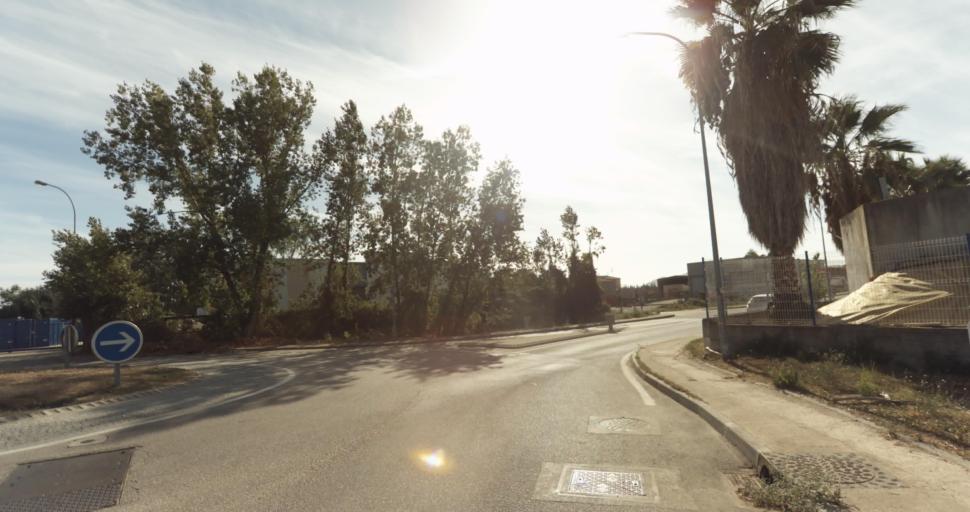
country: FR
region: Corsica
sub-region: Departement de la Corse-du-Sud
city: Afa
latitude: 41.9295
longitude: 8.7904
